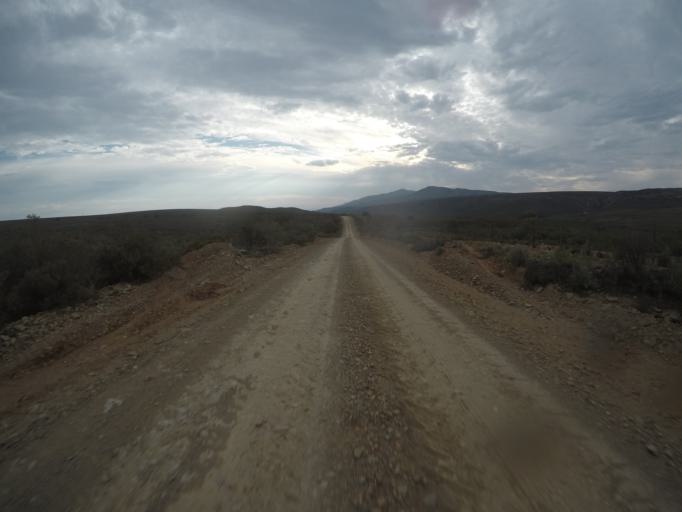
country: ZA
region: Eastern Cape
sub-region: Cacadu District Municipality
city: Willowmore
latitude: -33.4922
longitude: 23.5722
